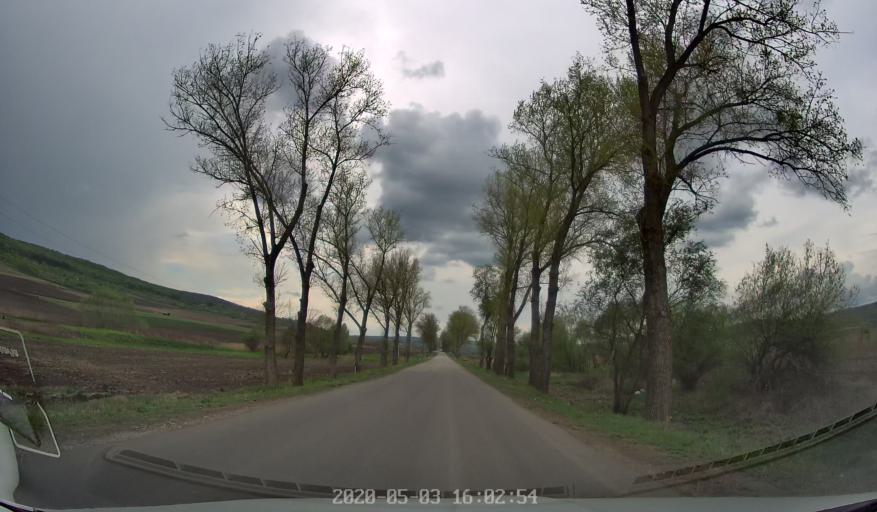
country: MD
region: Stinga Nistrului
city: Bucovat
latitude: 47.1762
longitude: 28.3890
